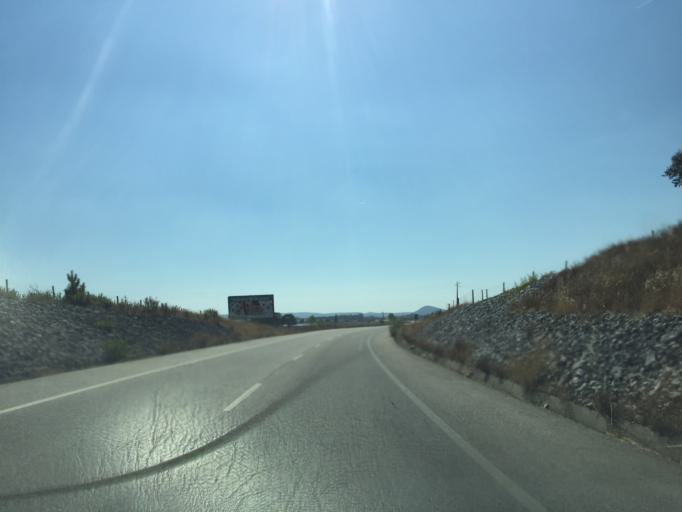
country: PT
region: Lisbon
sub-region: Azambuja
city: Aveiras de Cima
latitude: 39.1498
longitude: -8.8933
